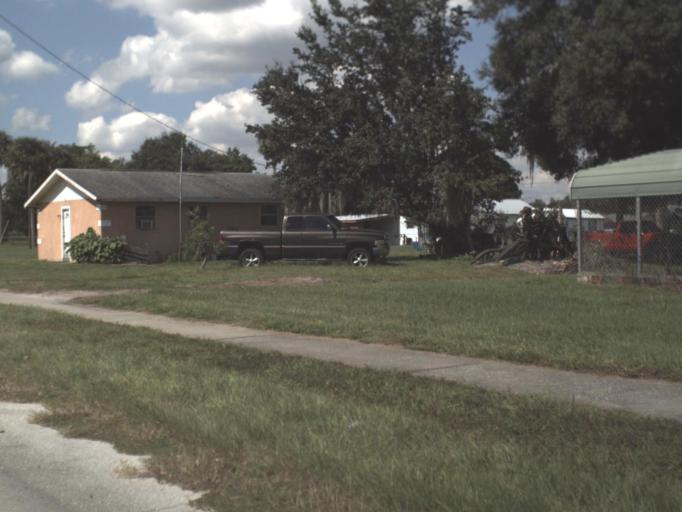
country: US
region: Florida
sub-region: Hardee County
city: Zolfo Springs
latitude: 27.4935
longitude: -81.7918
